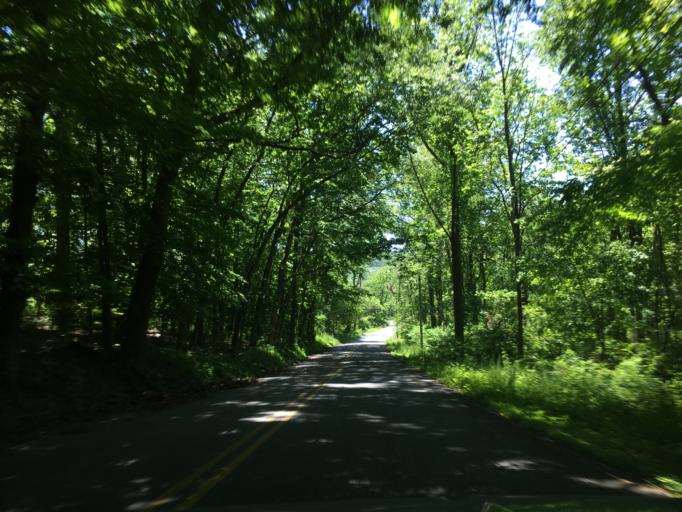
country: US
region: Pennsylvania
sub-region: Berks County
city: New Berlinville
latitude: 40.3672
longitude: -75.6607
